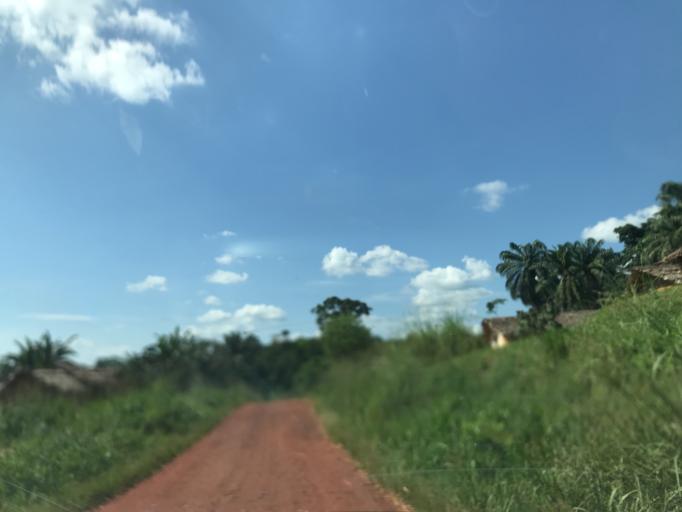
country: CD
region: Eastern Province
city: Kisangani
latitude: 1.2529
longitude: 25.2767
